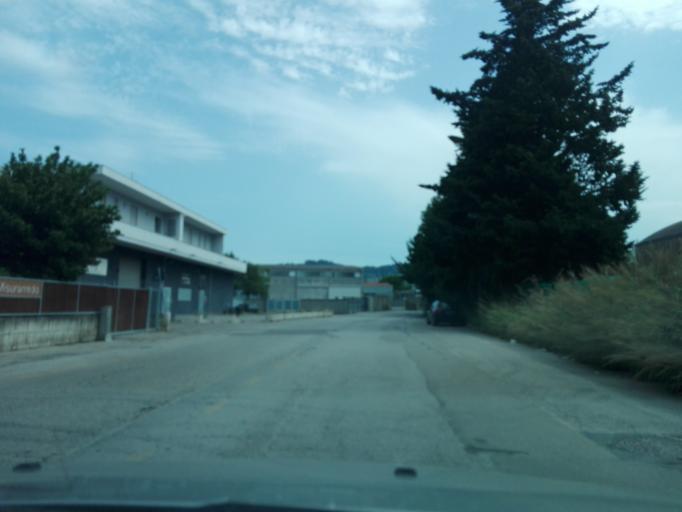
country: IT
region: Abruzzo
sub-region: Provincia di Pescara
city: Montesilvano Marina
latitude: 42.5084
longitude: 14.1300
